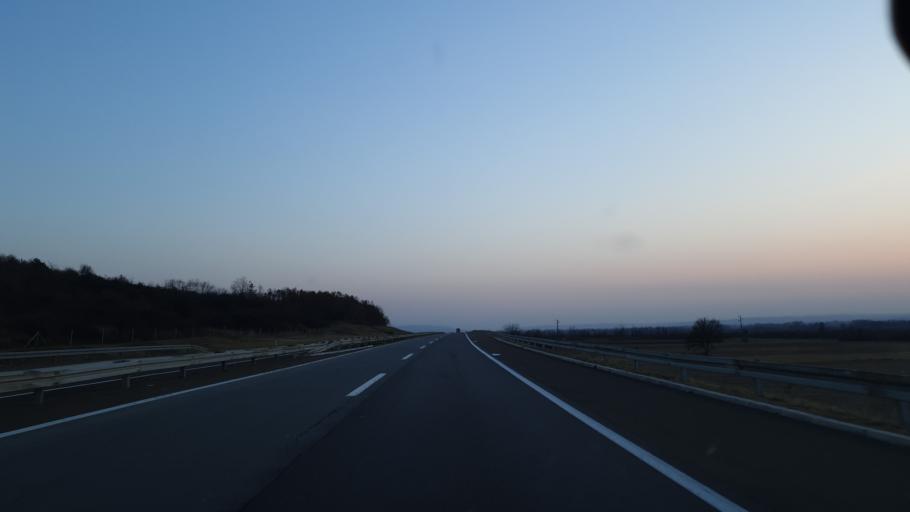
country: RS
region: Central Serbia
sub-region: Pomoravski Okrug
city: Paracin
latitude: 43.8236
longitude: 21.4284
